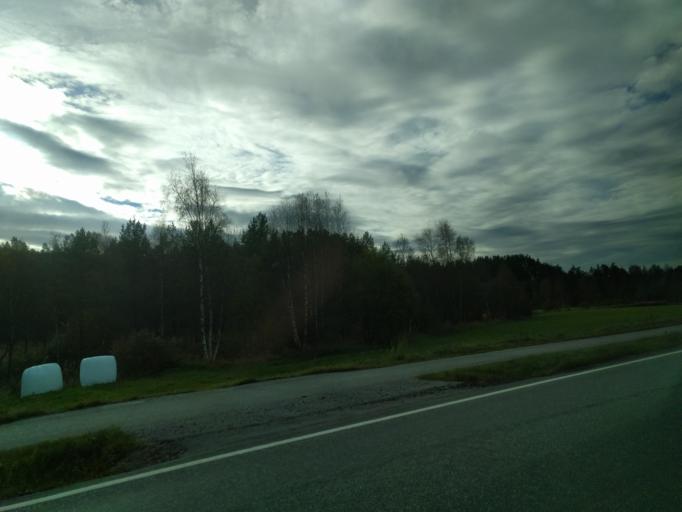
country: NO
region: Vest-Agder
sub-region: Songdalen
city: Nodeland
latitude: 58.2737
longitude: 7.8311
